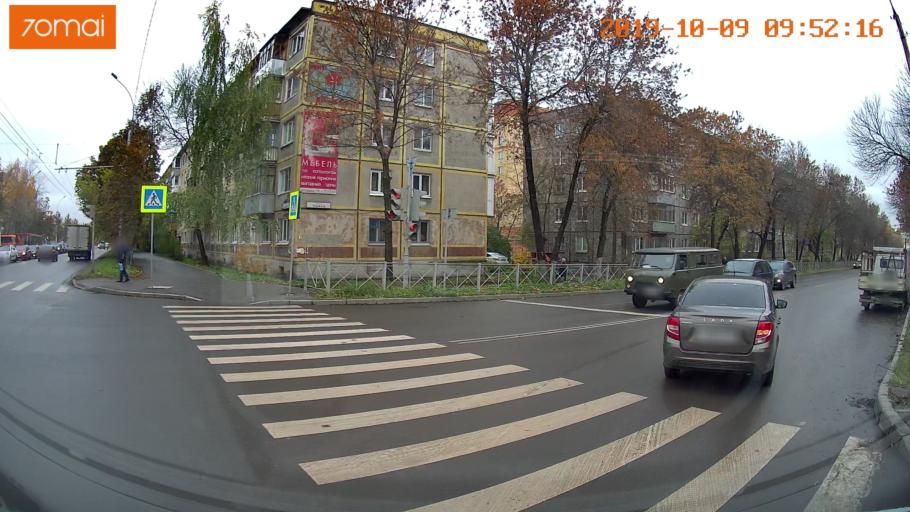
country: RU
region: Vologda
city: Vologda
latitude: 59.2064
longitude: 39.9039
